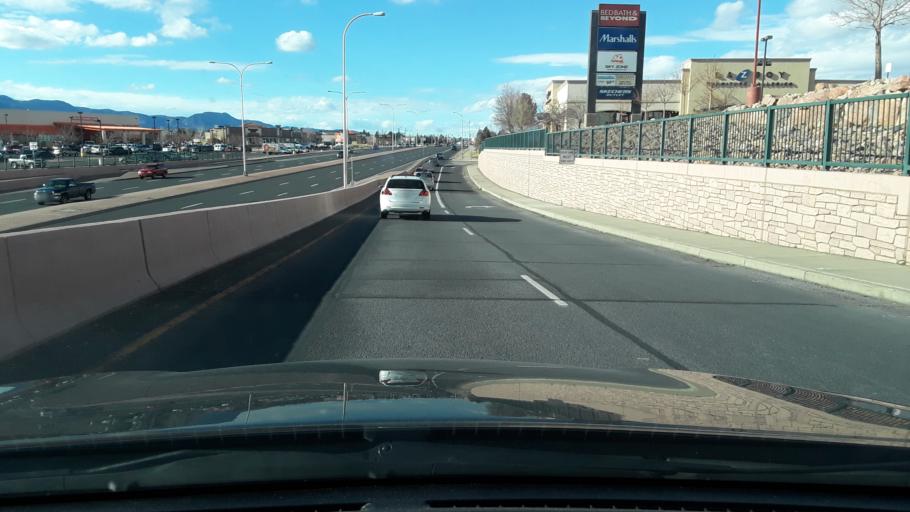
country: US
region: Colorado
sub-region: El Paso County
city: Air Force Academy
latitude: 38.9334
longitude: -104.7964
